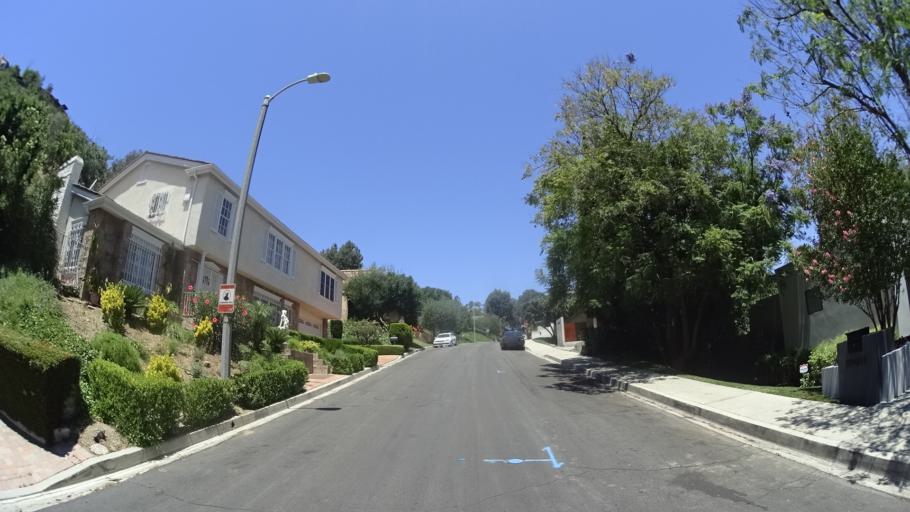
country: US
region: California
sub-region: Los Angeles County
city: Universal City
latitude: 34.1316
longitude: -118.3678
